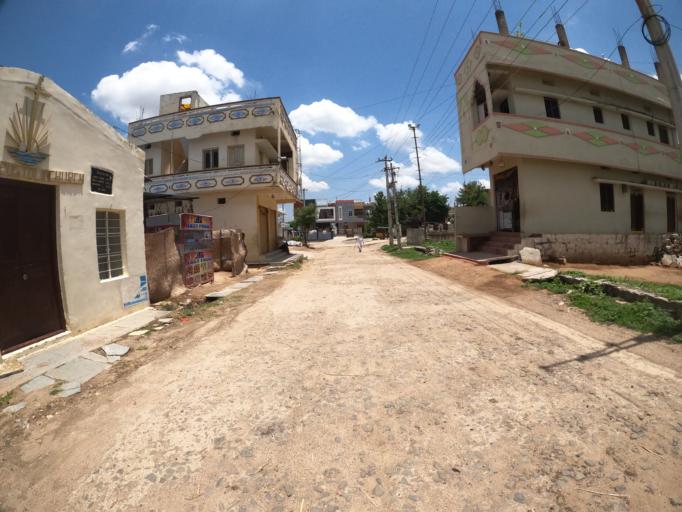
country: IN
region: Telangana
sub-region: Rangareddi
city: Singapur
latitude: 17.4409
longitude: 78.1573
